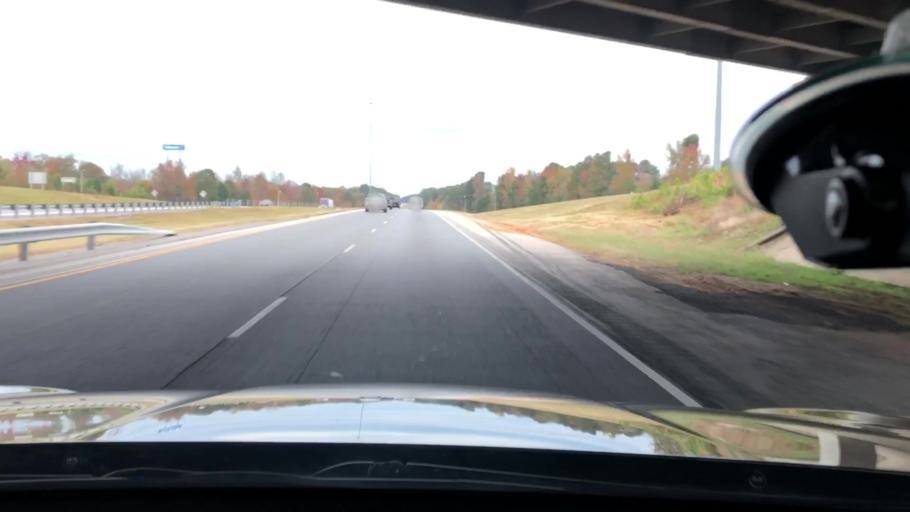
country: US
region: Arkansas
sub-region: Clark County
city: Arkadelphia
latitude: 34.1185
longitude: -93.0928
